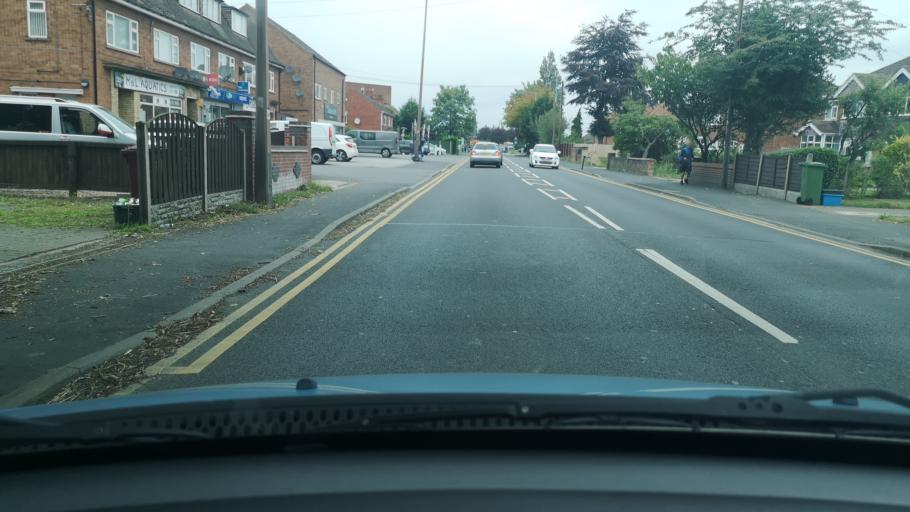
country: GB
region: England
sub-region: North Lincolnshire
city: Scunthorpe
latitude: 53.5881
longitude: -0.6839
